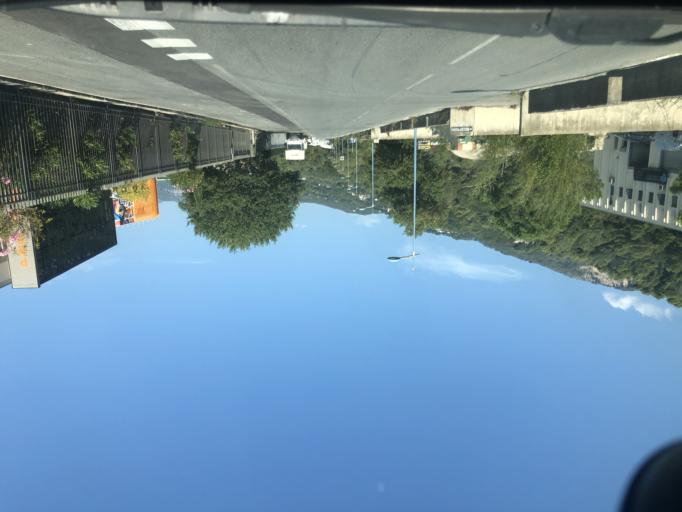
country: FR
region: Provence-Alpes-Cote d'Azur
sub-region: Departement des Alpes-Maritimes
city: Saint-Martin-du-Var
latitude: 43.8037
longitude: 7.1887
